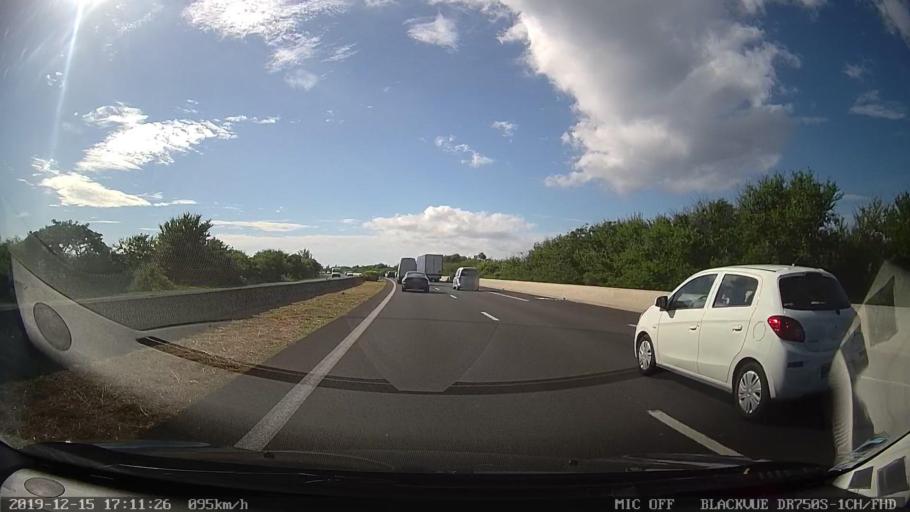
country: RE
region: Reunion
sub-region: Reunion
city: Les Avirons
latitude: -21.2767
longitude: 55.3415
